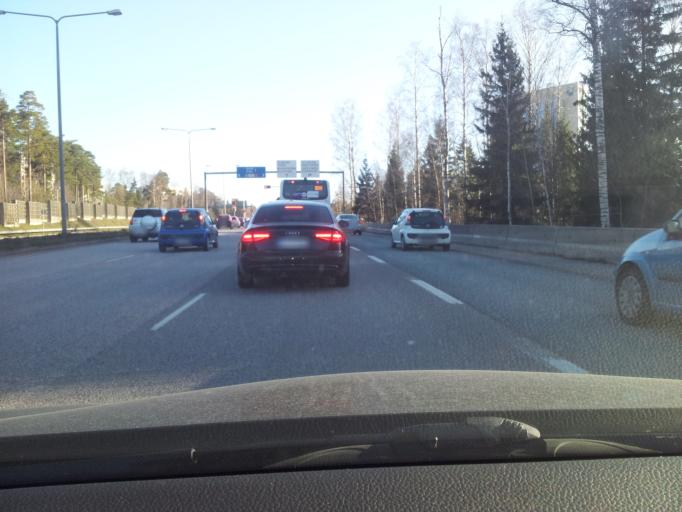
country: FI
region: Uusimaa
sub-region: Helsinki
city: Otaniemi
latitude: 60.1721
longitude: 24.8264
